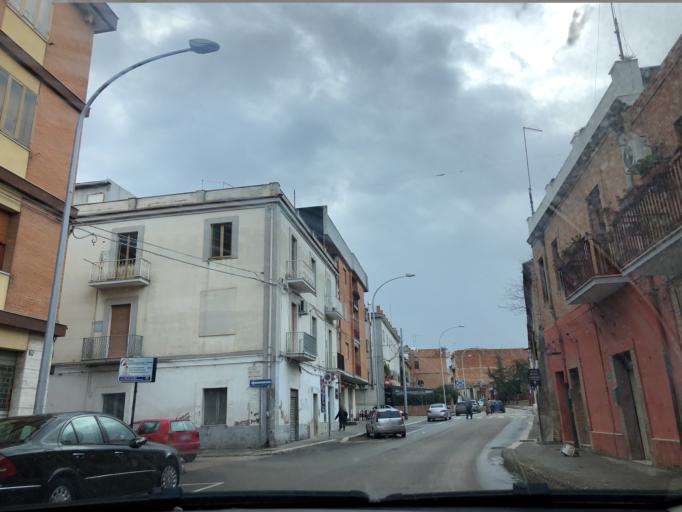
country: IT
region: Apulia
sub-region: Provincia di Foggia
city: Lucera
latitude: 41.5072
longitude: 15.3400
